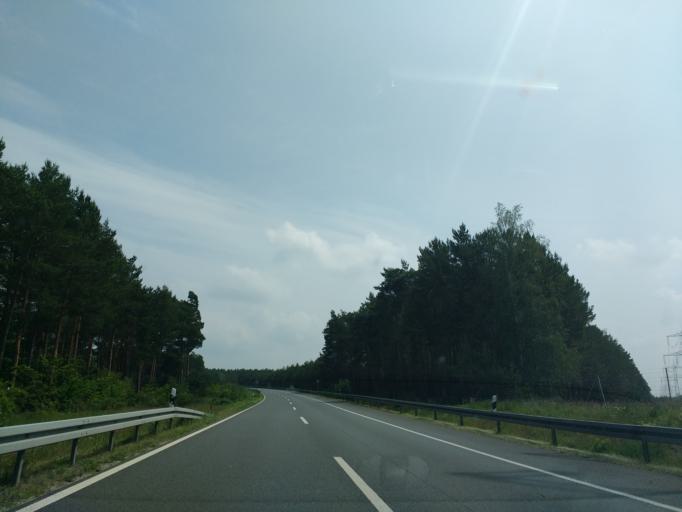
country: DE
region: Brandenburg
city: Gross Kreutz
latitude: 52.3377
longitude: 12.8038
